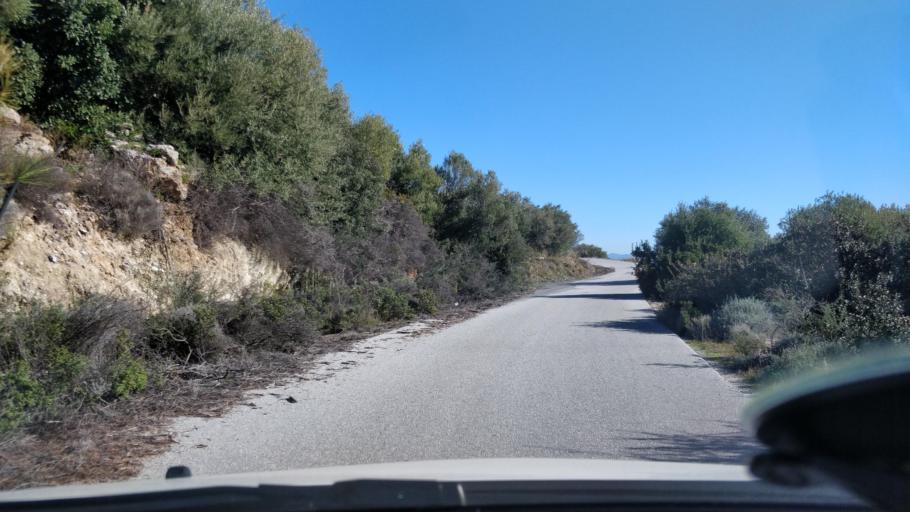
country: GR
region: Crete
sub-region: Nomos Lasithiou
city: Gra Liyia
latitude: 35.0189
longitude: 25.5502
